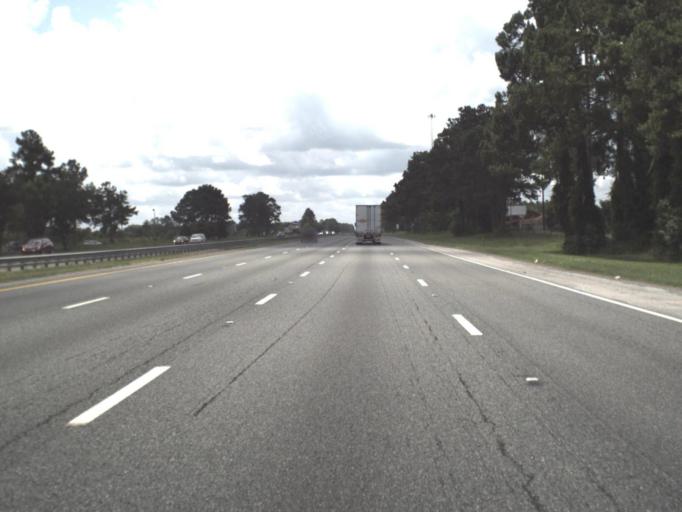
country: US
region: Florida
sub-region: Columbia County
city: Lake City
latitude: 30.1771
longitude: -82.6874
